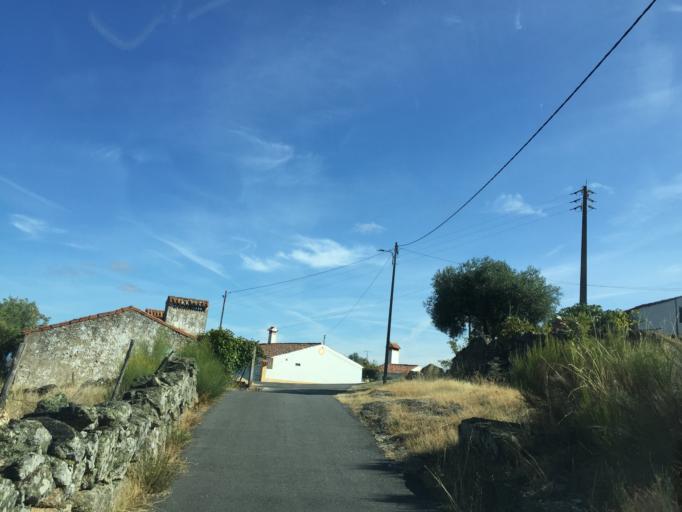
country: PT
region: Portalegre
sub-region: Marvao
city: Marvao
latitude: 39.3983
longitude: -7.3681
